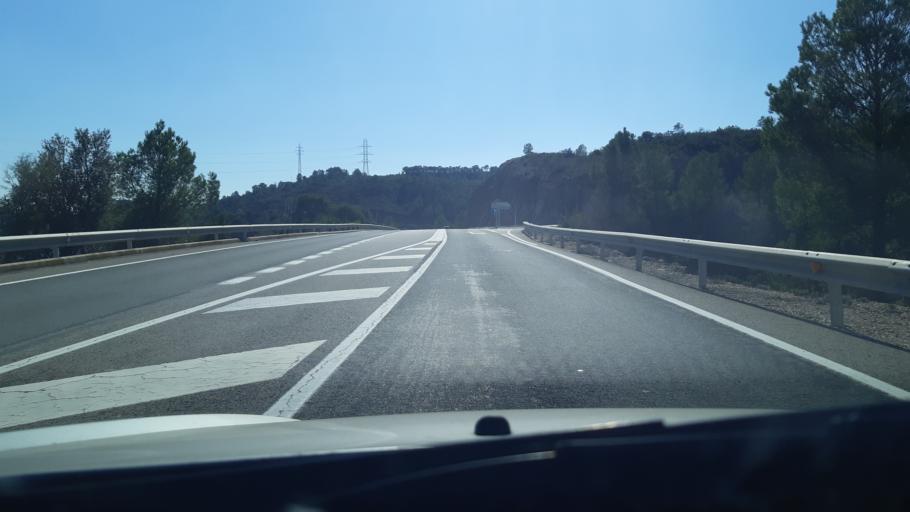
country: ES
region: Catalonia
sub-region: Provincia de Tarragona
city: Tivenys
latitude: 40.9333
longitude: 0.4850
